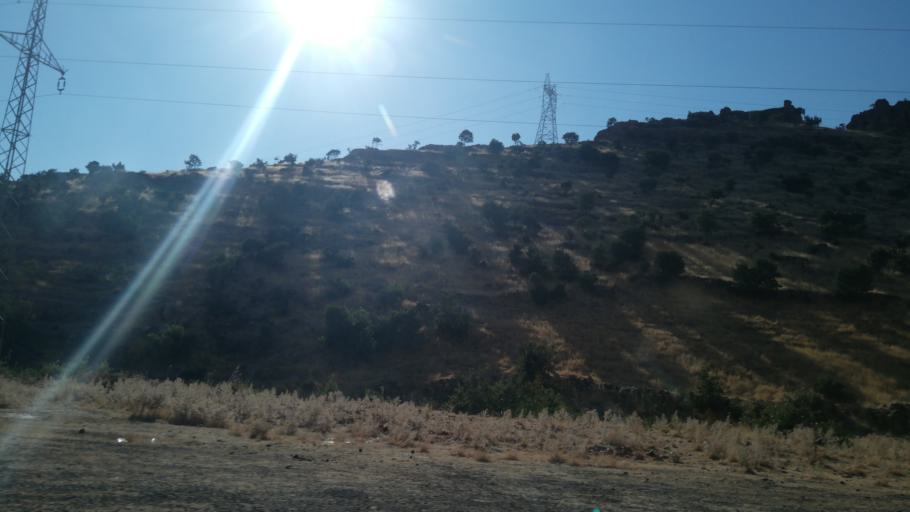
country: TR
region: Mardin
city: Sivrice
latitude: 37.2490
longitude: 41.3560
